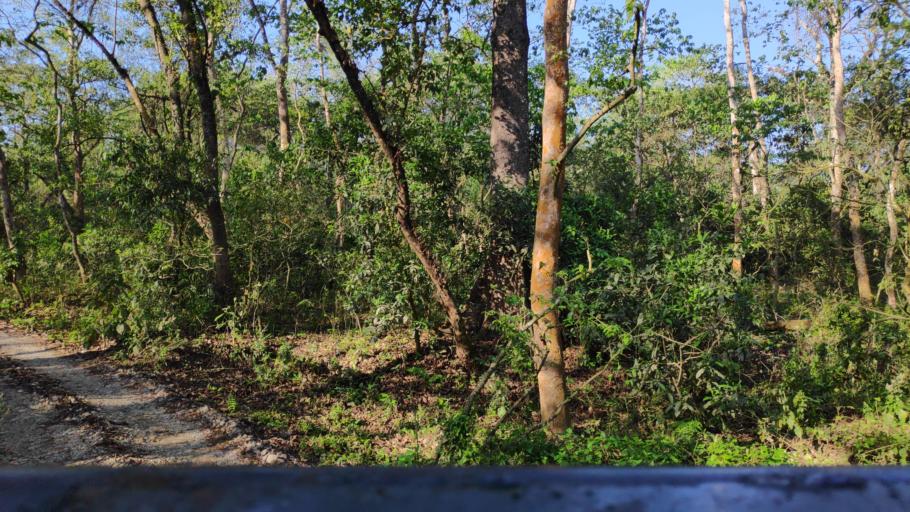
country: NP
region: Central Region
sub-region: Narayani Zone
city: Bharatpur
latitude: 27.5614
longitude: 84.5348
